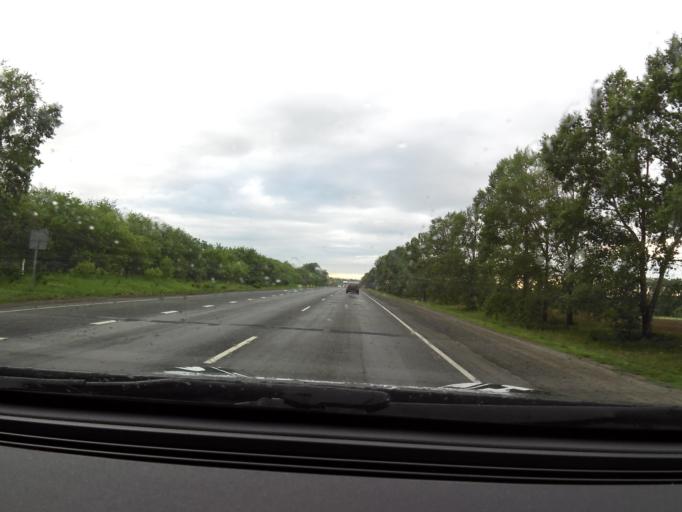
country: RU
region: Chuvashia
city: Yantikovo
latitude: 55.7897
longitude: 47.7009
